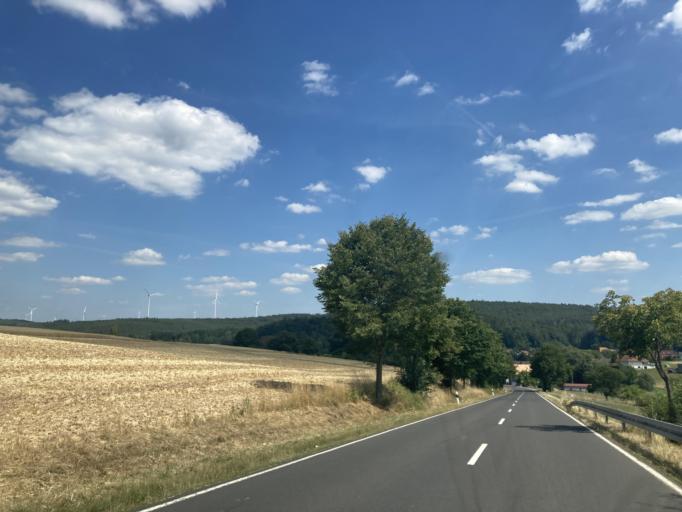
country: DE
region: Hesse
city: Grebenau
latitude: 50.7164
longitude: 9.4392
